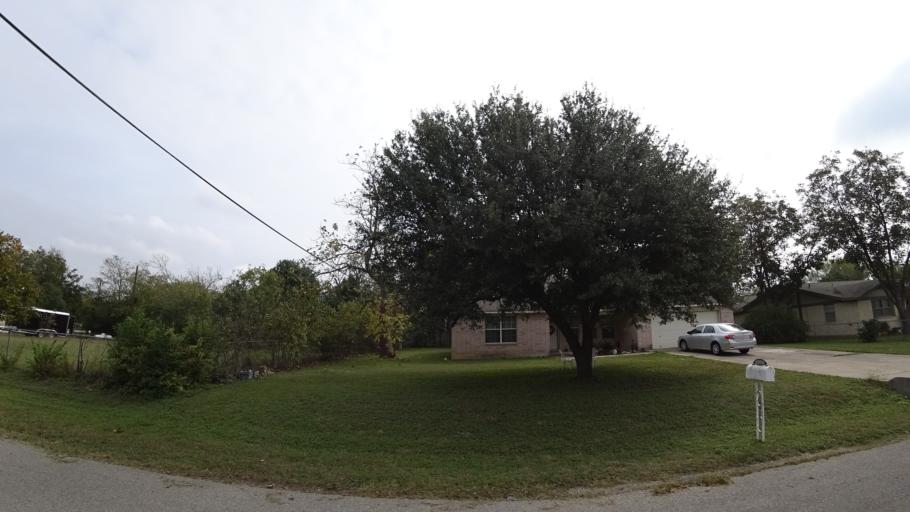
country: US
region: Texas
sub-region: Williamson County
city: Round Rock
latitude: 30.4955
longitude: -97.6886
